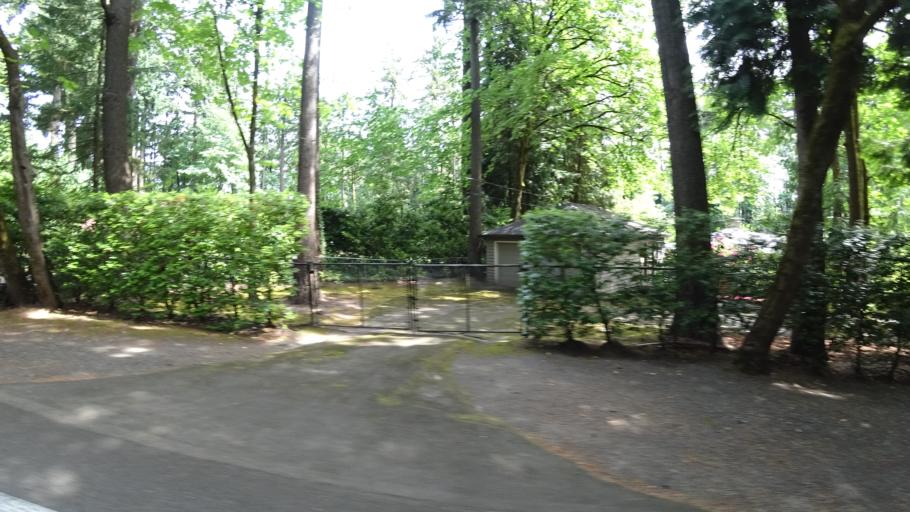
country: US
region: Oregon
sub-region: Clackamas County
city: Lake Oswego
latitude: 45.4406
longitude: -122.6626
